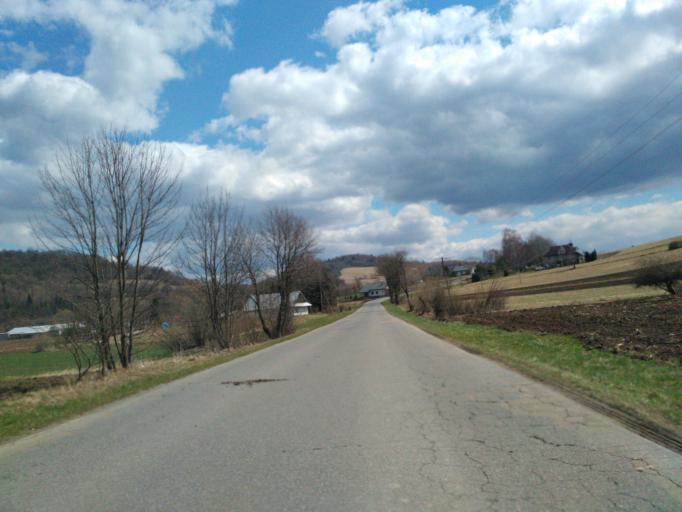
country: PL
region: Subcarpathian Voivodeship
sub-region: Powiat sanocki
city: Tyrawa Woloska
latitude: 49.5796
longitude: 22.3564
